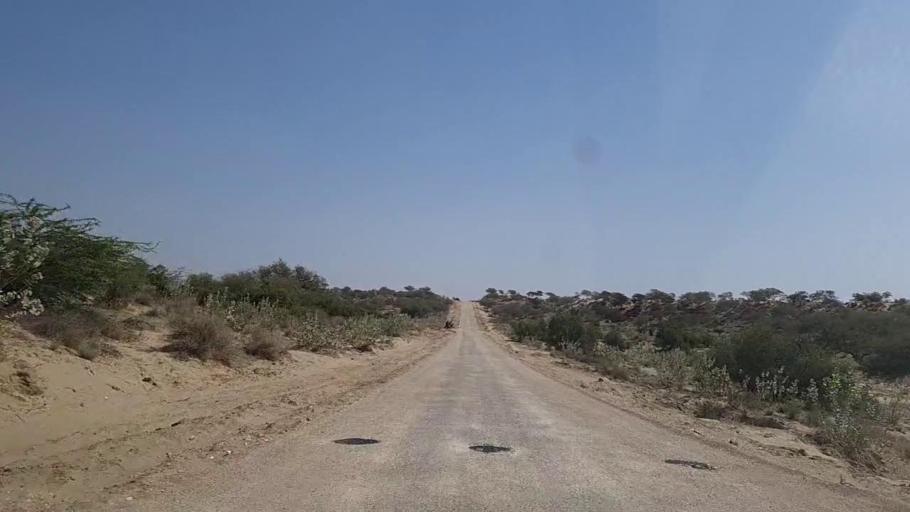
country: PK
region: Sindh
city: Diplo
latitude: 24.4784
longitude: 69.5024
